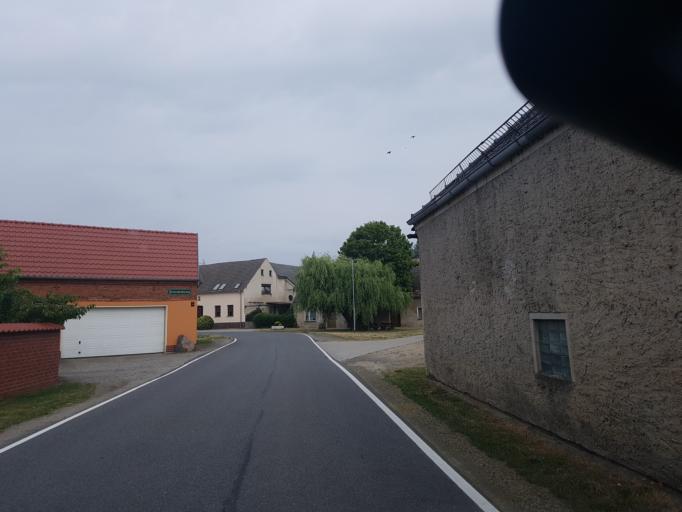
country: DE
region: Brandenburg
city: Schonewalde
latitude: 51.7021
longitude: 13.6025
